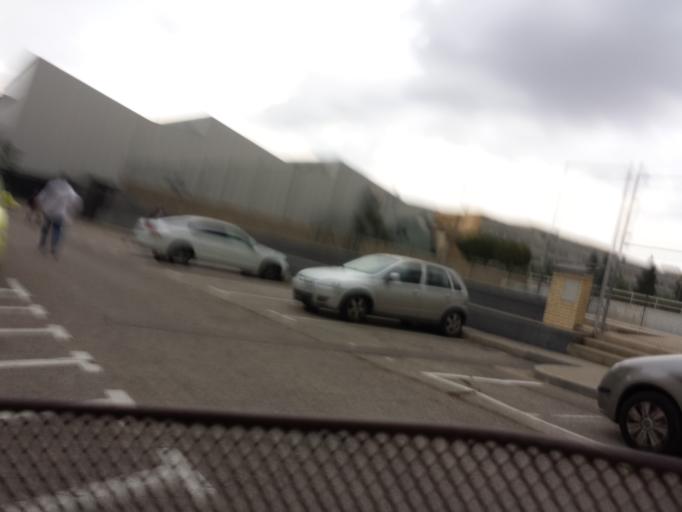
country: ES
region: Aragon
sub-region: Provincia de Zaragoza
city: Delicias
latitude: 41.6444
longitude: -0.9003
